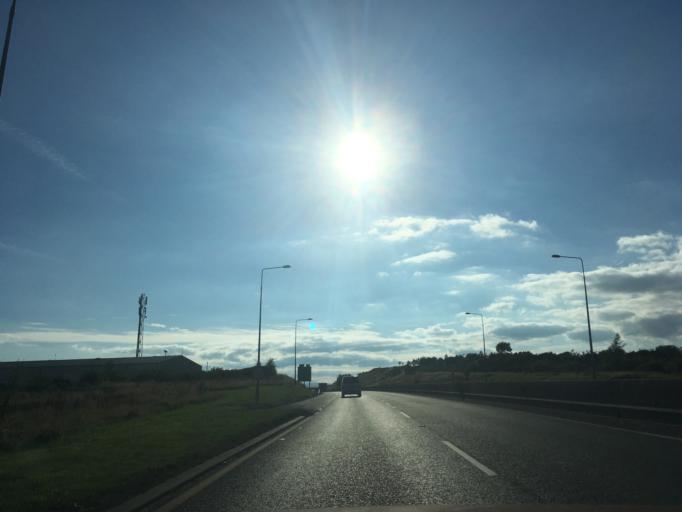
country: IE
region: Munster
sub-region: Waterford
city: Waterford
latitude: 52.2908
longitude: -7.0613
